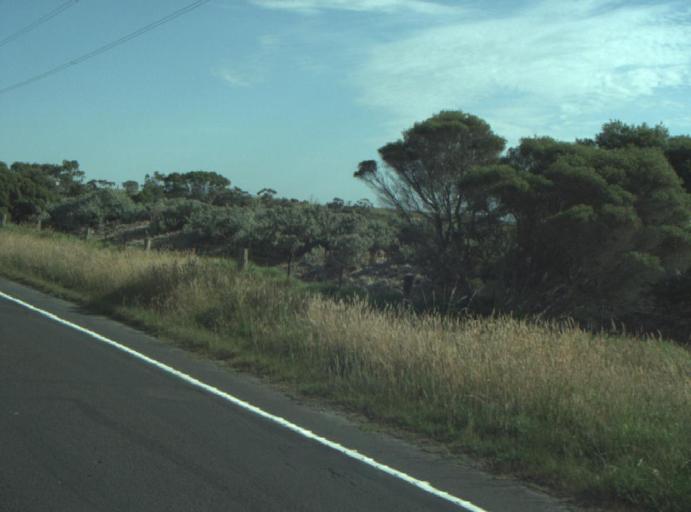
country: AU
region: Victoria
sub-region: Greater Geelong
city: East Geelong
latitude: -38.1456
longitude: 144.4298
